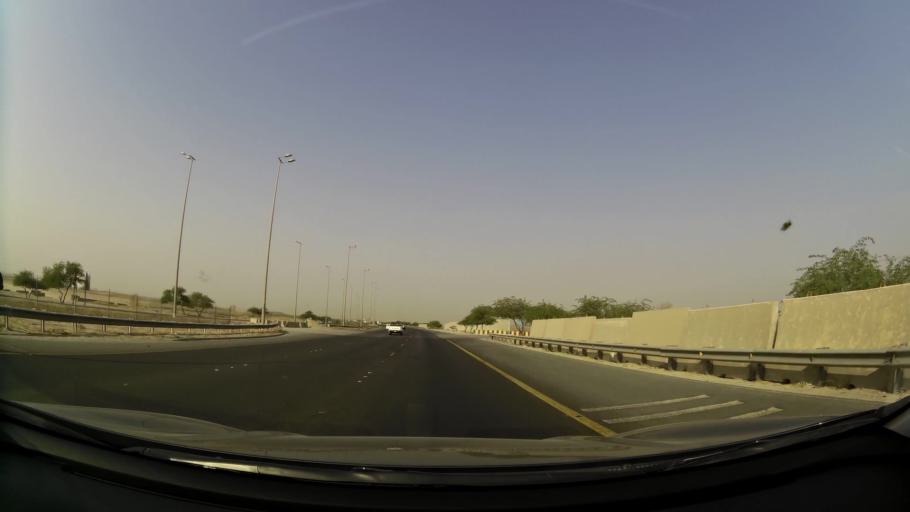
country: KW
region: Mubarak al Kabir
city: Mubarak al Kabir
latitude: 29.1826
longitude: 48.0217
